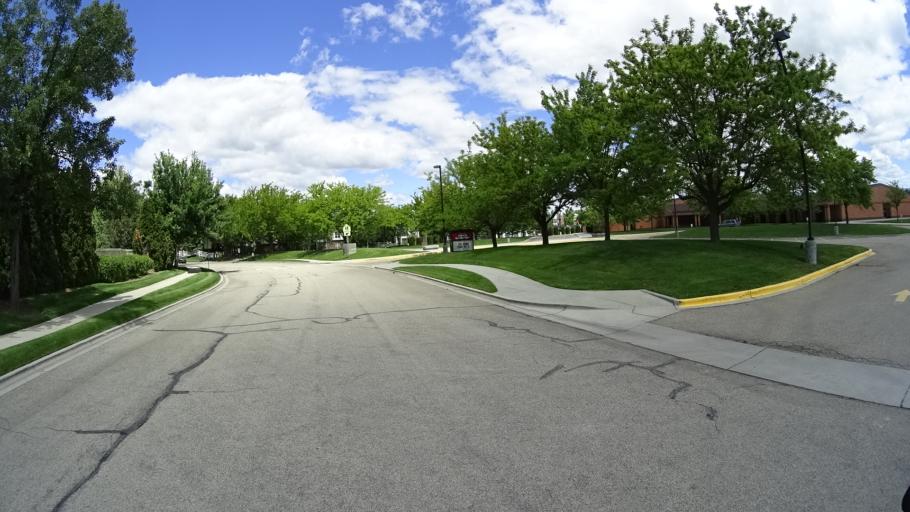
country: US
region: Idaho
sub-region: Ada County
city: Eagle
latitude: 43.6599
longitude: -116.3455
